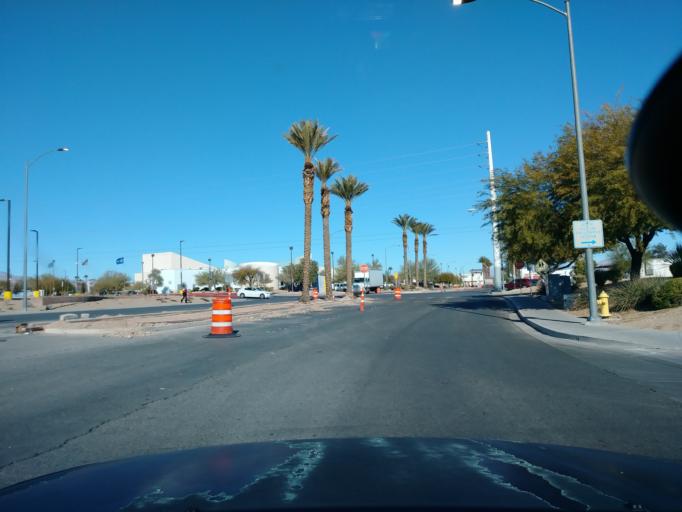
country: US
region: Nevada
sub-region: Clark County
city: Spring Valley
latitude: 36.1567
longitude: -115.2301
